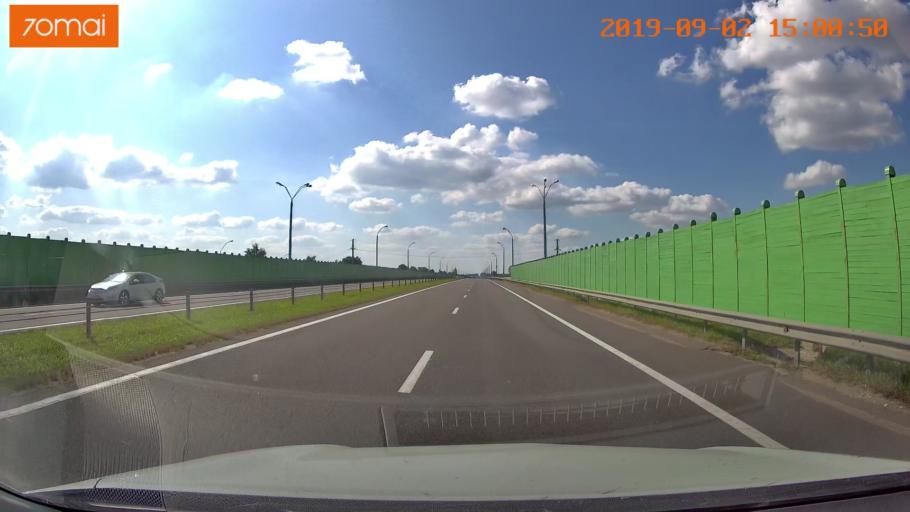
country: BY
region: Mogilev
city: Vishow
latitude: 53.9785
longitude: 30.0649
